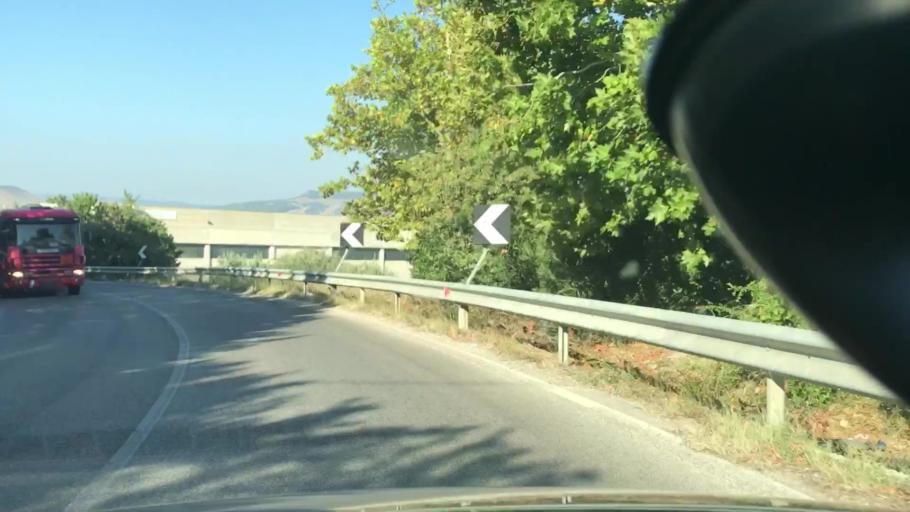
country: IT
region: Basilicate
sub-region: Provincia di Matera
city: La Martella
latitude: 40.6606
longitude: 16.5631
